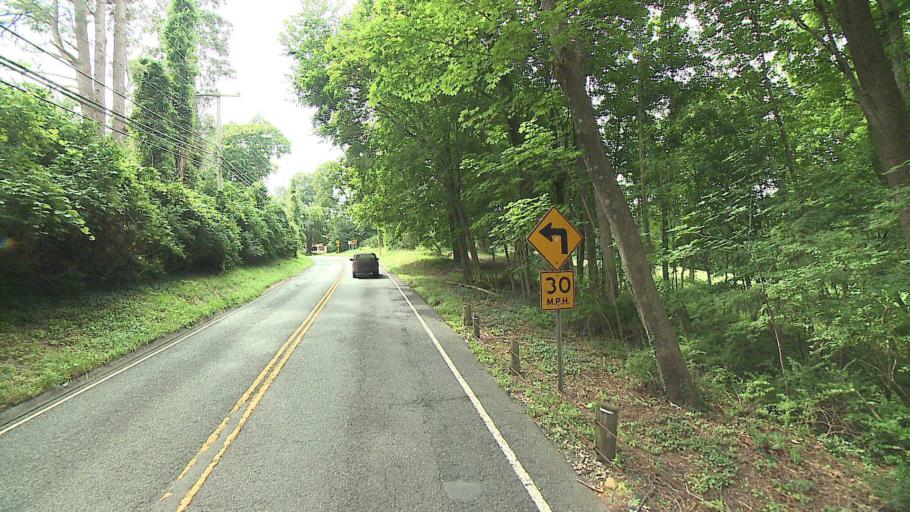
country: US
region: Connecticut
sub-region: Litchfield County
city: New Preston
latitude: 41.6324
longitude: -73.3142
